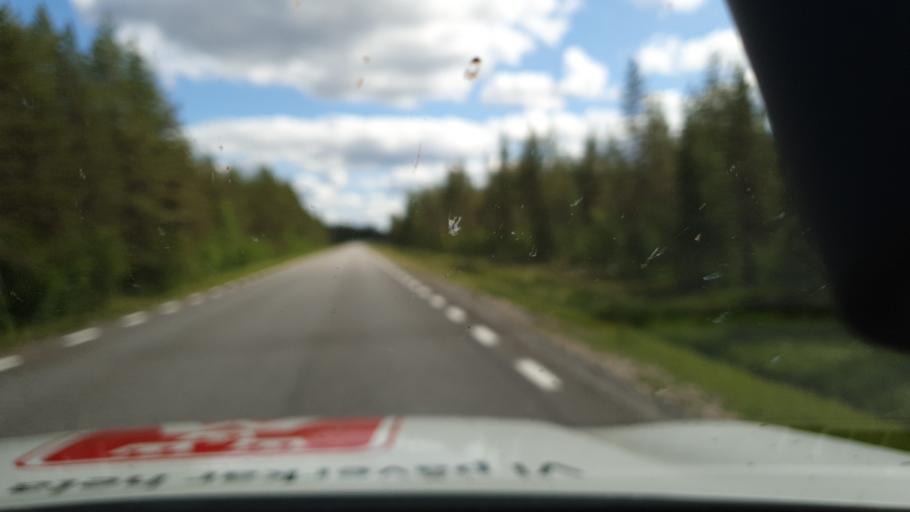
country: SE
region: Norrbotten
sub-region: Arjeplogs Kommun
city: Arjeplog
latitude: 65.5421
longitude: 18.2179
